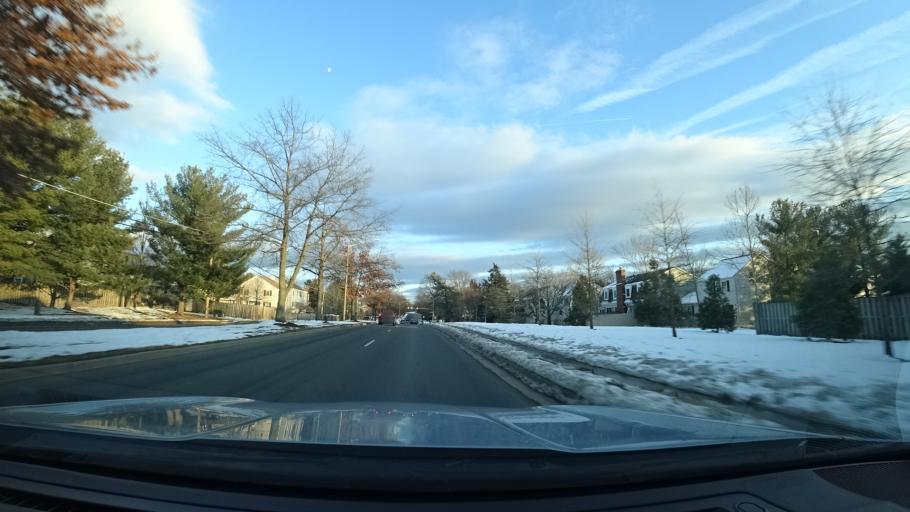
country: US
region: Virginia
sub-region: Fairfax County
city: Herndon
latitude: 38.9605
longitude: -77.3962
